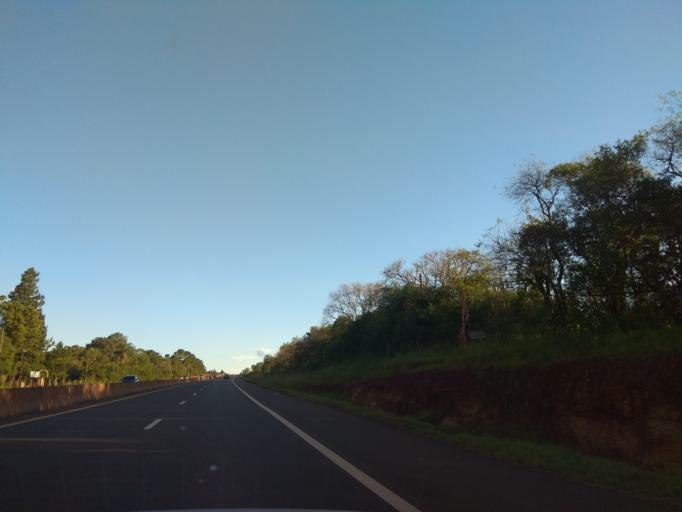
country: AR
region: Misiones
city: Garupa
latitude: -27.5138
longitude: -55.8600
